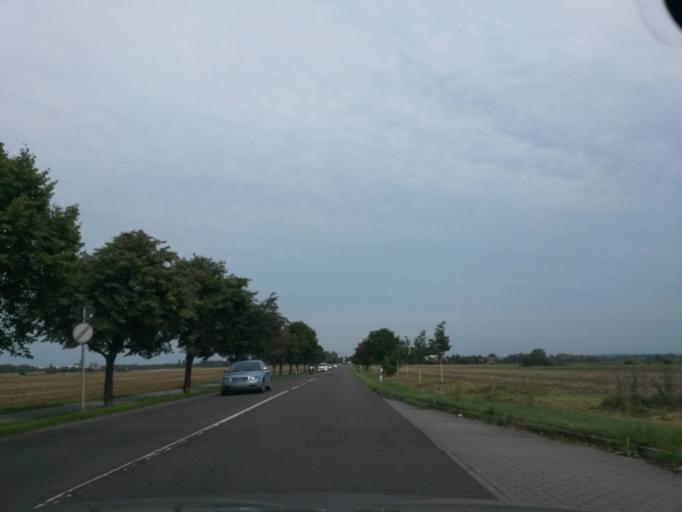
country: DE
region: Brandenburg
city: Meyenburg
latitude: 53.0416
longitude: 14.2593
